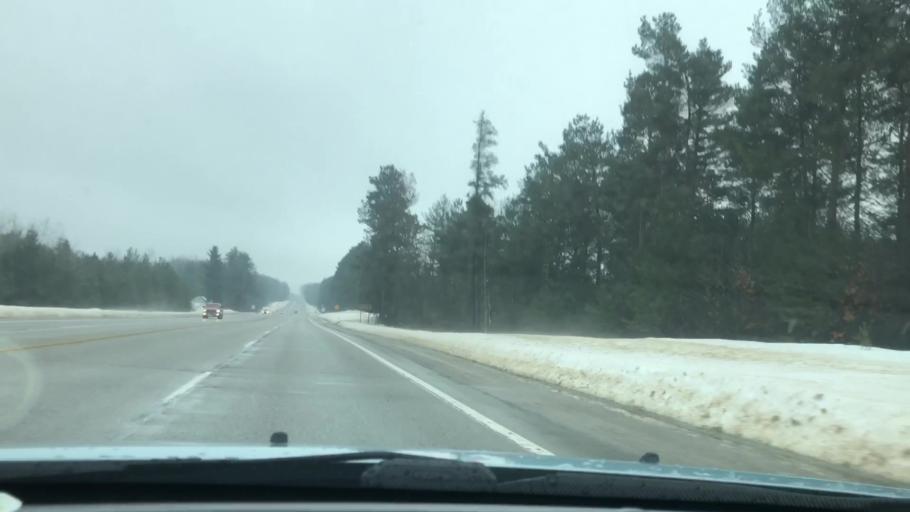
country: US
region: Michigan
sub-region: Otsego County
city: Gaylord
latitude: 45.0450
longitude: -84.7759
